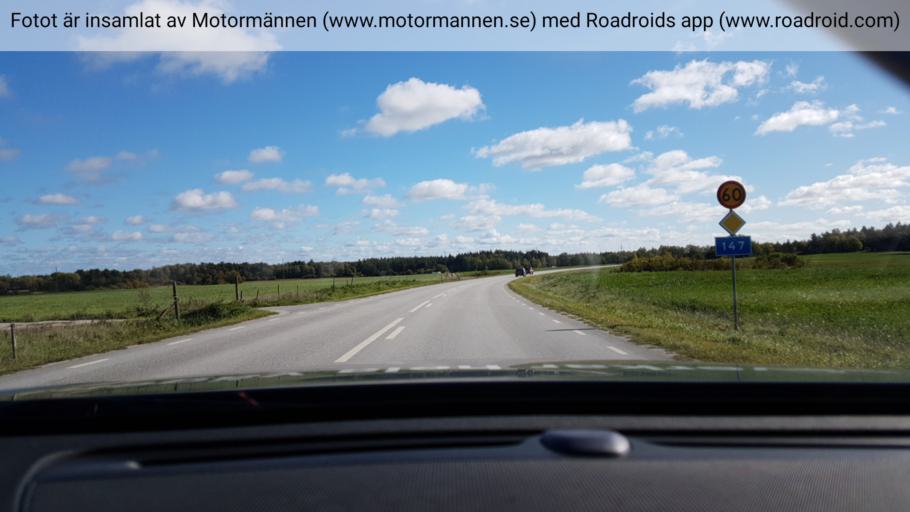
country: SE
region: Gotland
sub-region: Gotland
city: Slite
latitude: 57.7736
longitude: 18.7780
